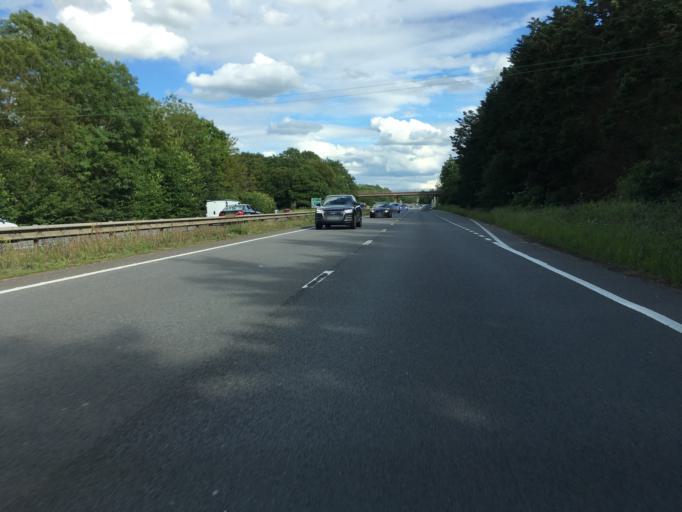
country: GB
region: England
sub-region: Oxfordshire
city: Wheatley
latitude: 51.7420
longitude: -1.1096
